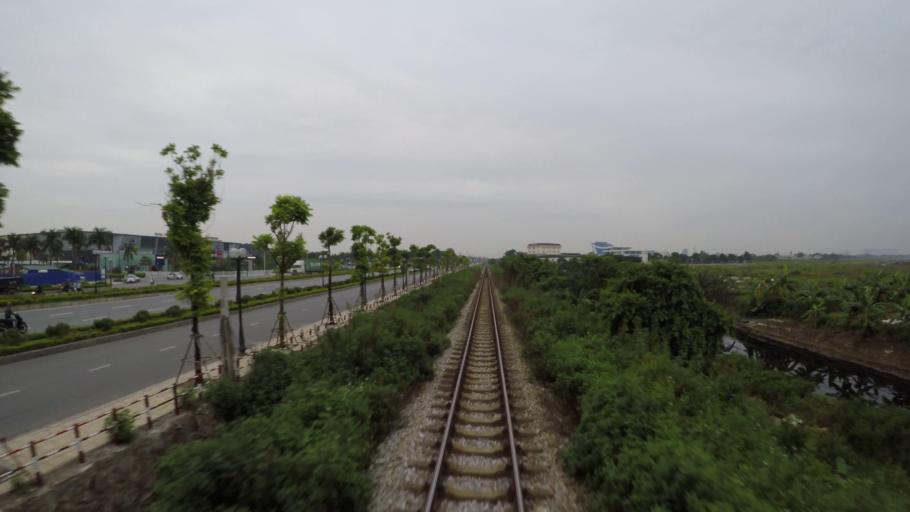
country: VN
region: Ha Noi
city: Trau Quy
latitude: 21.0158
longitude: 105.9455
